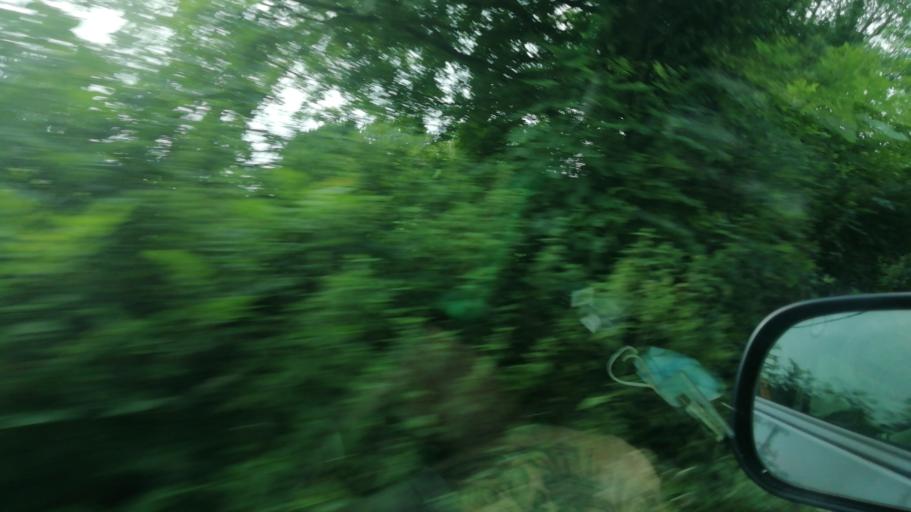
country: IE
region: Munster
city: Fethard
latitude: 52.5828
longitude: -7.6151
